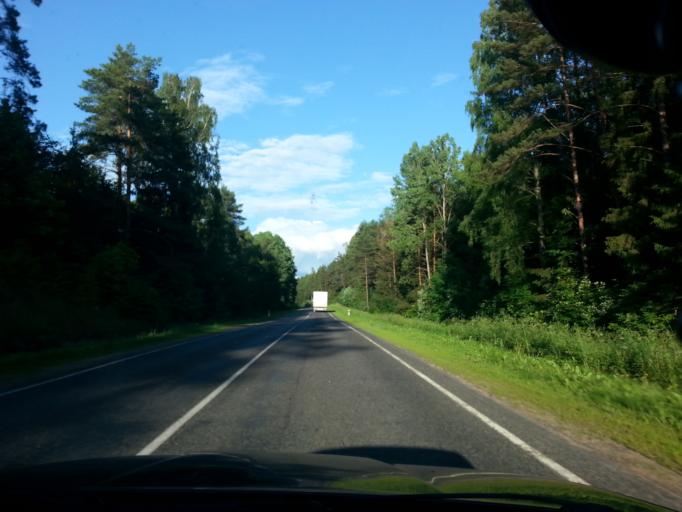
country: BY
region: Minsk
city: Svir
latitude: 54.8558
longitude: 26.2989
